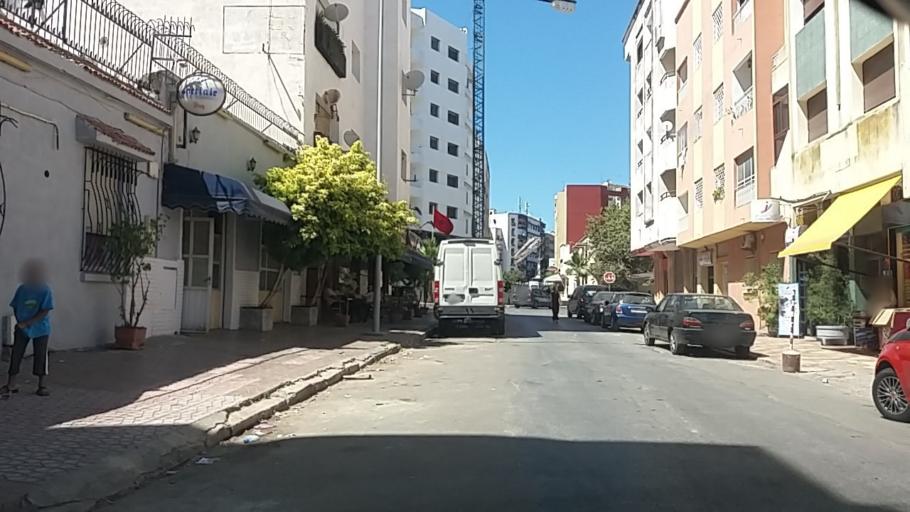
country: MA
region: Gharb-Chrarda-Beni Hssen
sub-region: Kenitra Province
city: Kenitra
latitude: 34.2599
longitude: -6.5872
